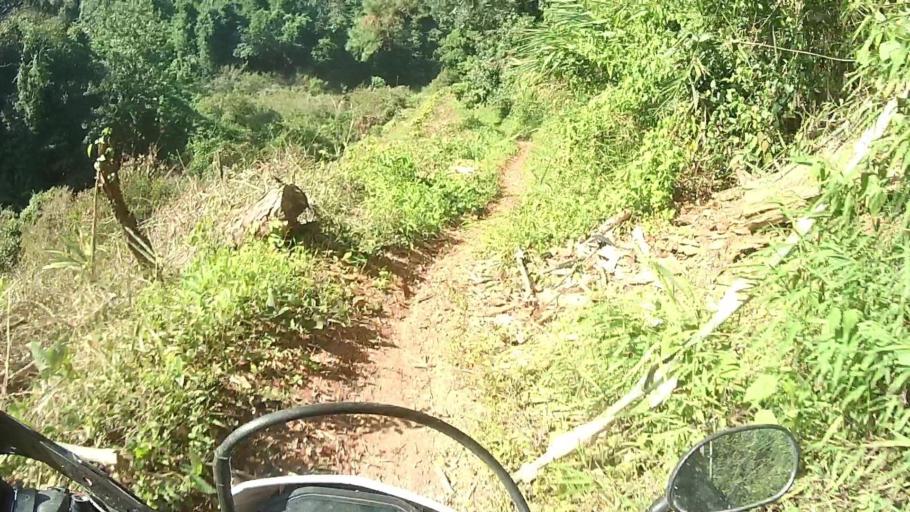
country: TH
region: Chiang Mai
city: Phrao
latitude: 19.3731
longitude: 99.3185
